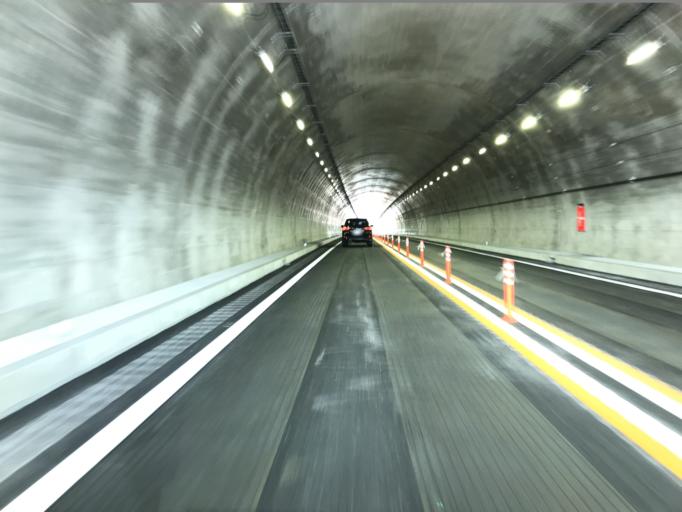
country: JP
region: Yamagata
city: Kaminoyama
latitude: 38.1017
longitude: 140.2168
